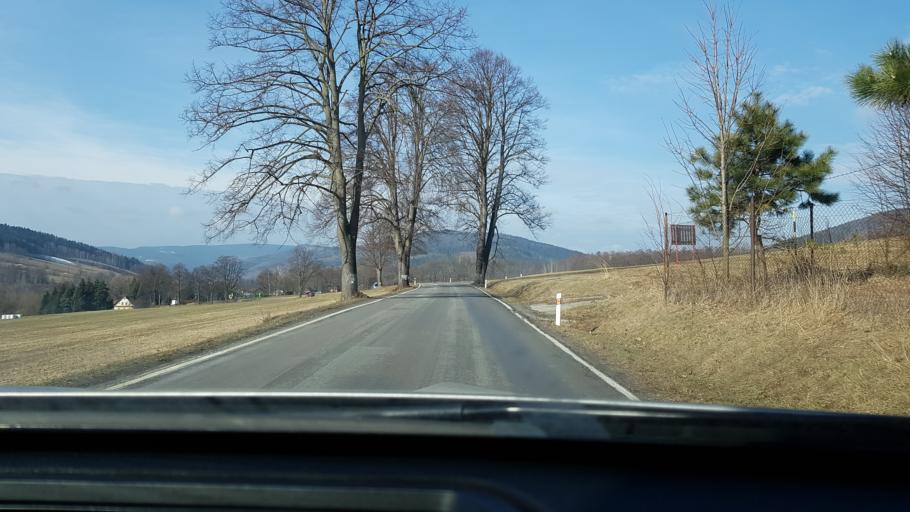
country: CZ
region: Olomoucky
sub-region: Okres Jesenik
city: Jesenik
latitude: 50.2284
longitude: 17.1764
